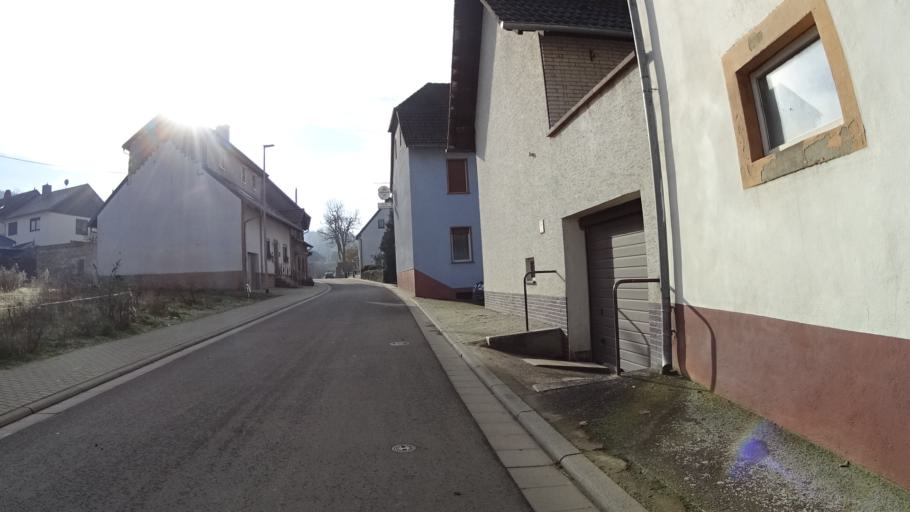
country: DE
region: Rheinland-Pfalz
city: Wiesweiler
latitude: 49.6378
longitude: 7.5725
